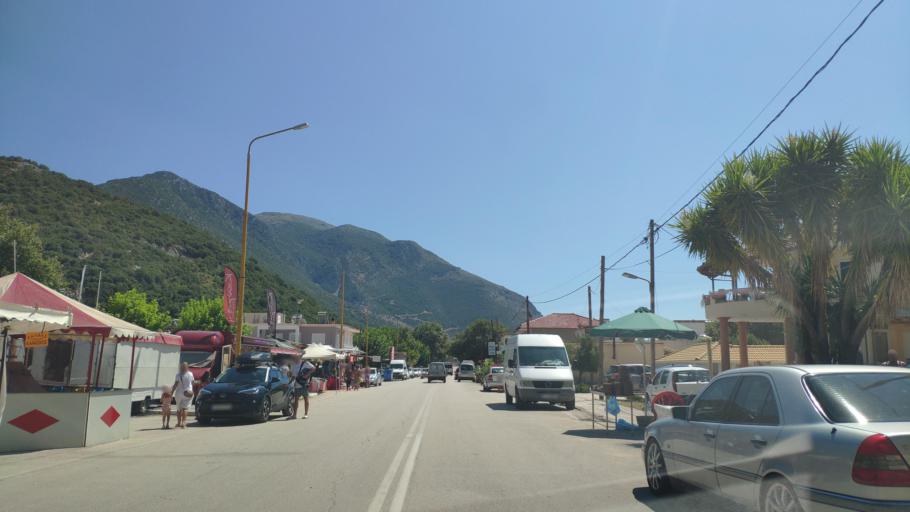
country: GR
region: Epirus
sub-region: Nomos Prevezis
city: Kanalaki
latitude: 39.3254
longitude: 20.6073
